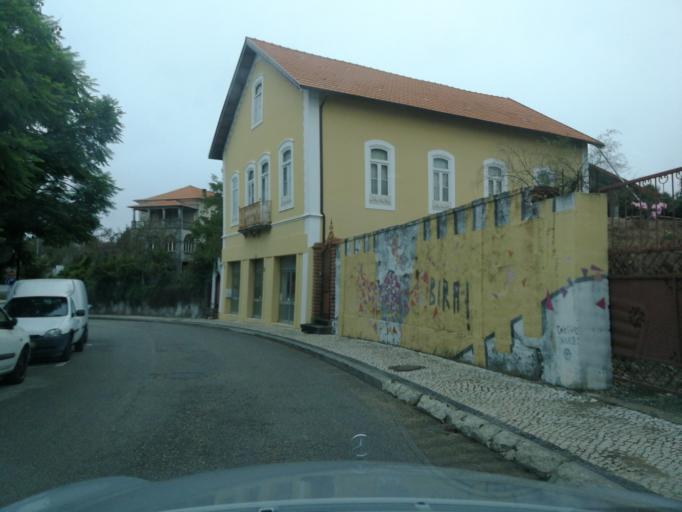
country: PT
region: Aveiro
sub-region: Agueda
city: Agueda
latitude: 40.5739
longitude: -8.4475
